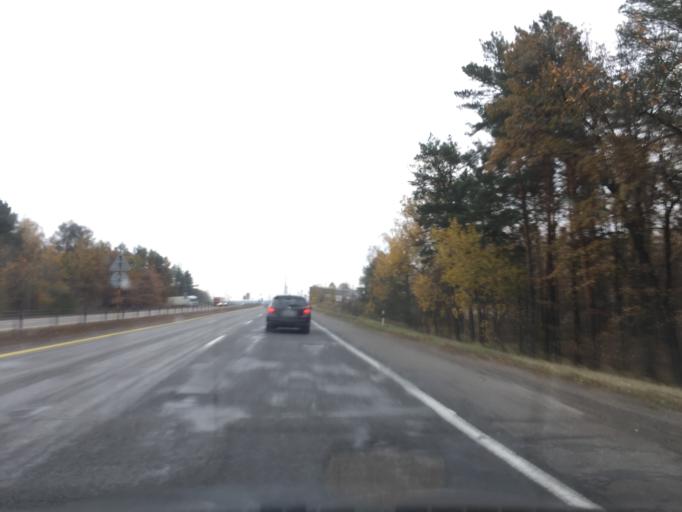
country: BY
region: Gomel
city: Horad Rechytsa
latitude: 52.3299
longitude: 30.5384
